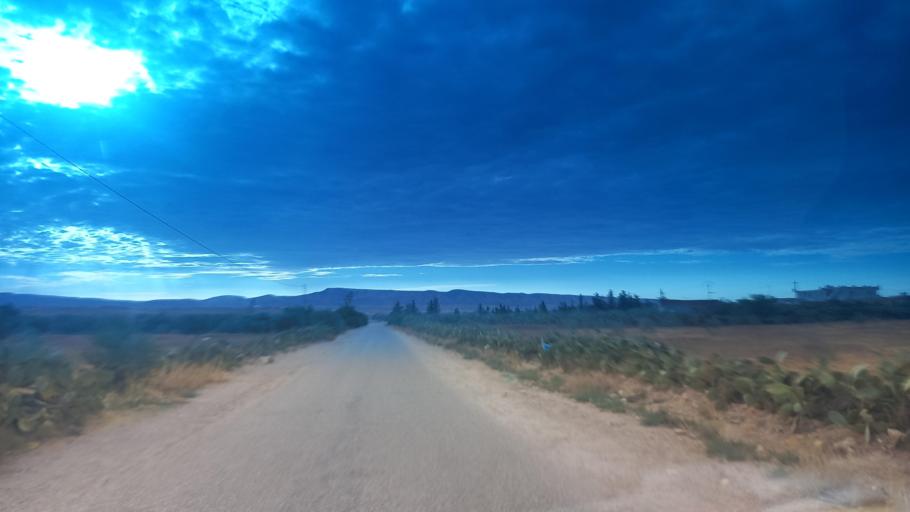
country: TN
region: Al Qasrayn
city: Sbiba
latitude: 35.3824
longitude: 9.0489
